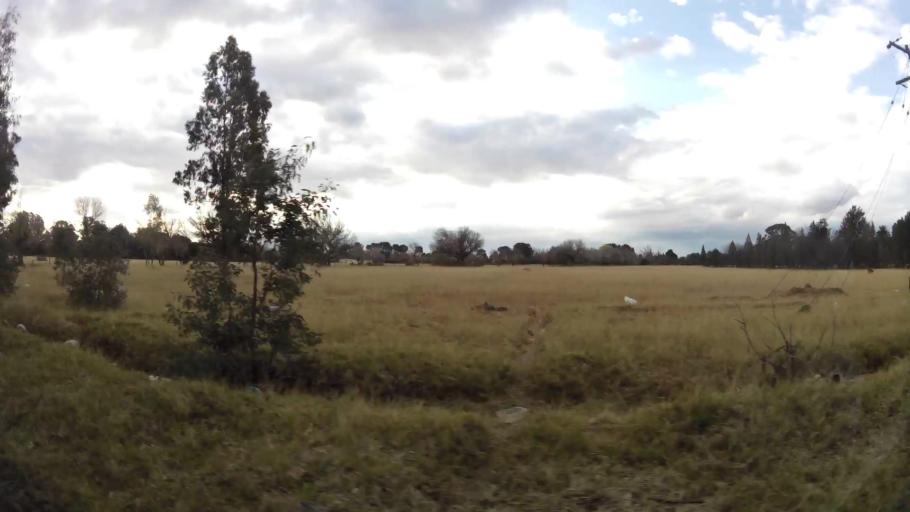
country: ZA
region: Orange Free State
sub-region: Lejweleputswa District Municipality
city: Welkom
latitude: -28.0002
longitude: 26.7168
